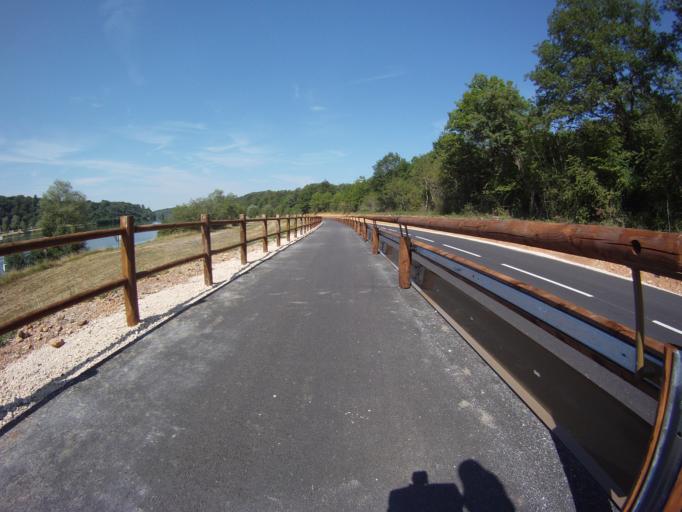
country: FR
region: Lorraine
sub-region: Departement de Meurthe-et-Moselle
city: Liverdun
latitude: 48.7588
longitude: 6.0349
